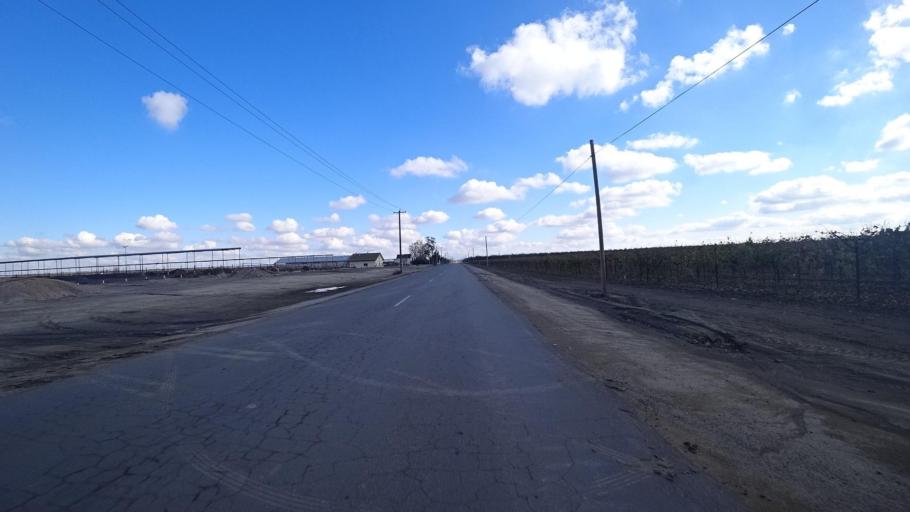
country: US
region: California
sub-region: Kern County
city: McFarland
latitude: 35.6887
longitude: -119.2717
